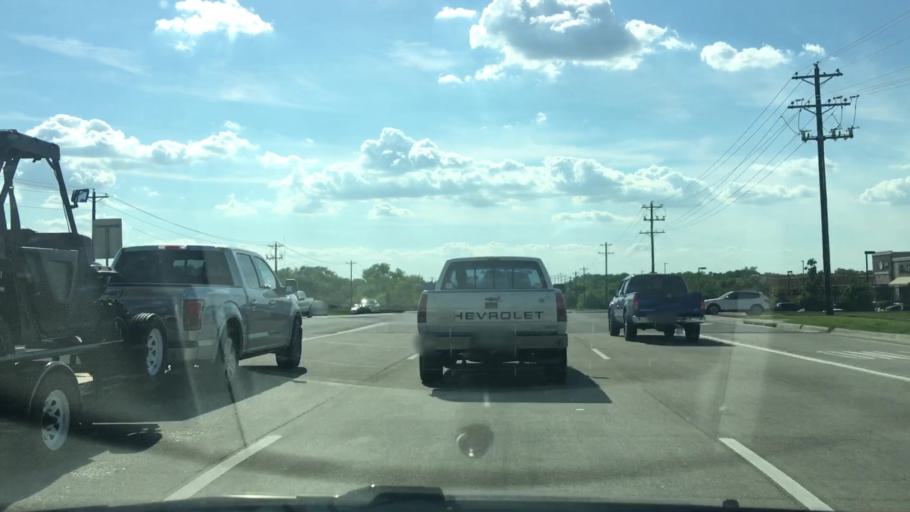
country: US
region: Texas
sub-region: Collin County
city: Prosper
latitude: 33.2186
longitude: -96.7344
